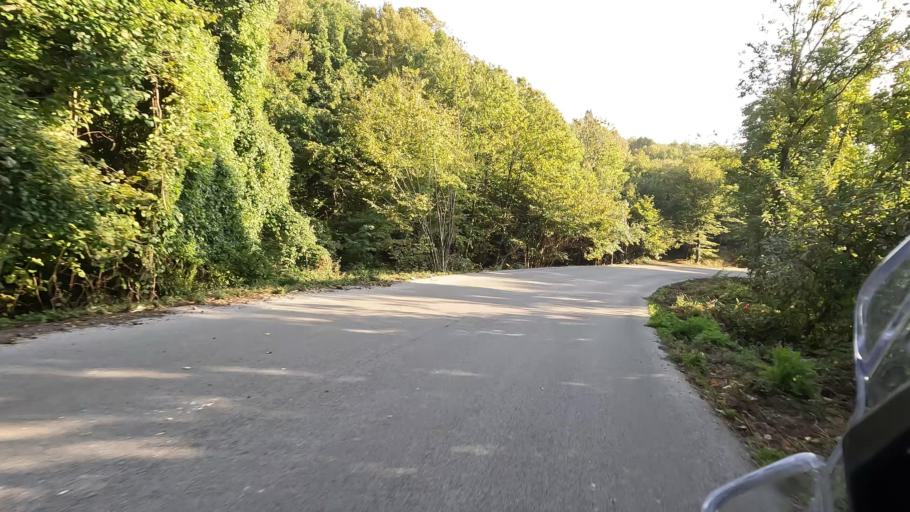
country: IT
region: Liguria
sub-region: Provincia di Savona
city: San Giovanni
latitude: 44.4124
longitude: 8.5293
